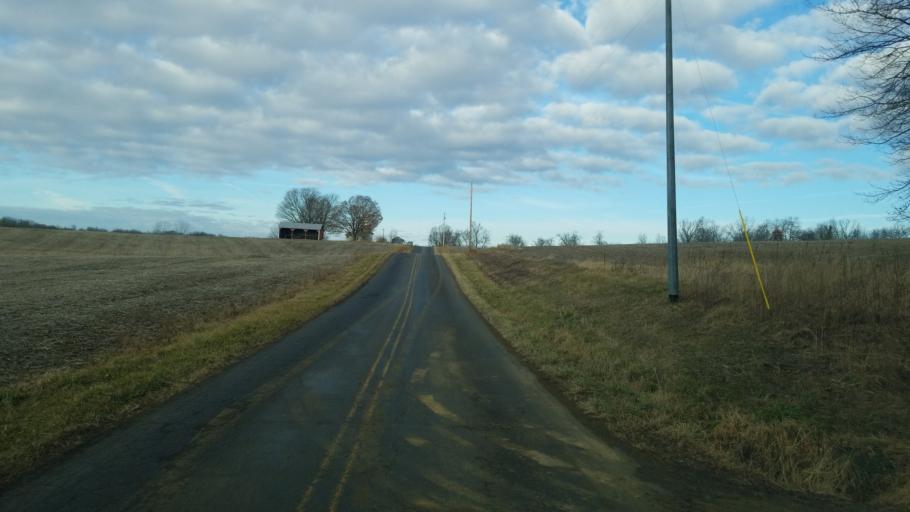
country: US
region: Ohio
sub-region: Knox County
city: Oak Hill
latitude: 40.3173
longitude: -82.2979
